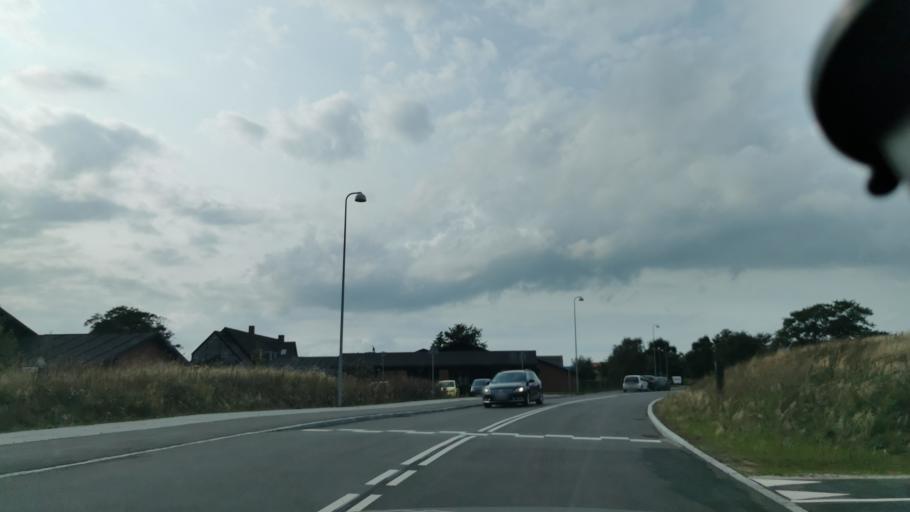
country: DK
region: Zealand
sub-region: Kalundborg Kommune
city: Kalundborg
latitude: 55.6956
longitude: 11.0688
